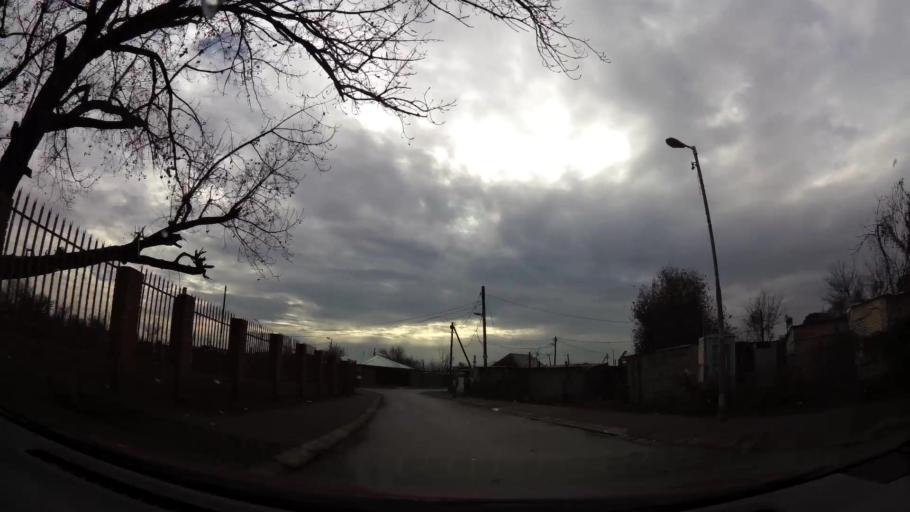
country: ZA
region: Gauteng
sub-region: City of Johannesburg Metropolitan Municipality
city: Soweto
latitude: -26.2867
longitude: 27.8414
